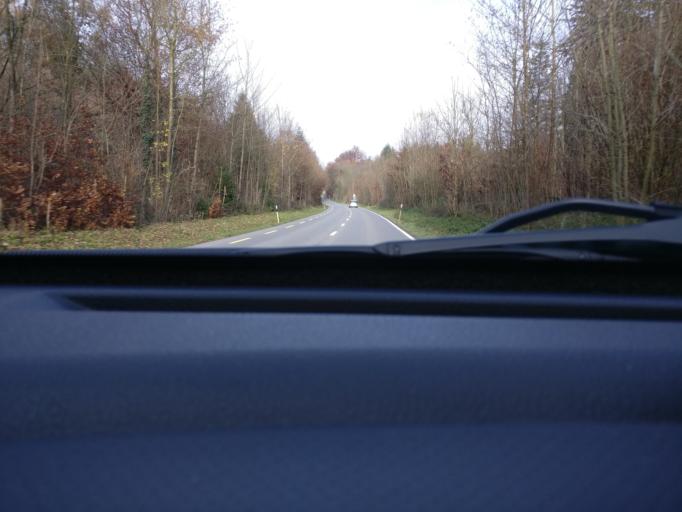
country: CH
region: Bern
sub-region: Bern-Mittelland District
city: Bolligen
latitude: 46.9964
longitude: 7.4876
